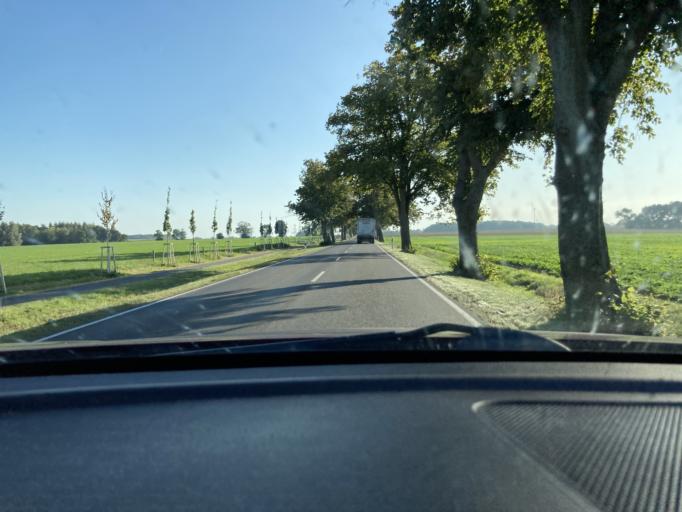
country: DE
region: Mecklenburg-Vorpommern
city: Anklam
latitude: 53.7955
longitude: 13.6672
